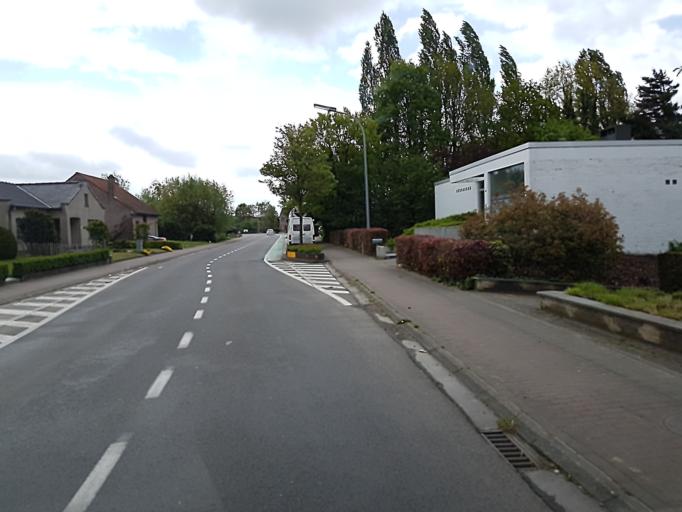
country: BE
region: Flanders
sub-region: Provincie Vlaams-Brabant
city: Londerzeel
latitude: 50.9989
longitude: 4.2993
